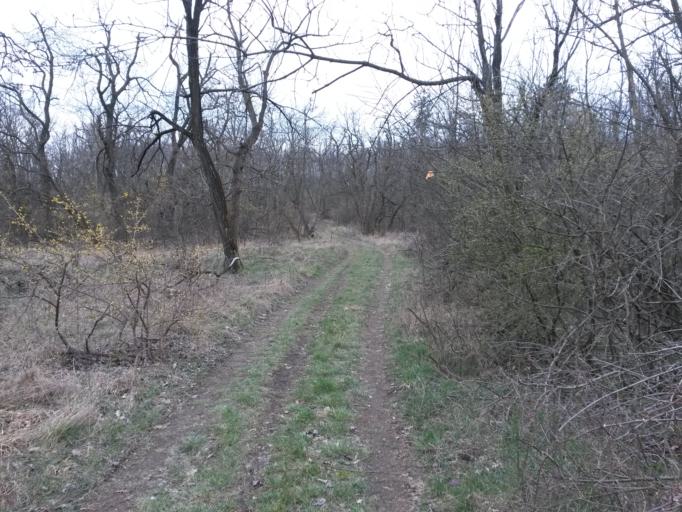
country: HU
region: Pest
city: Telki
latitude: 47.5817
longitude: 18.8461
